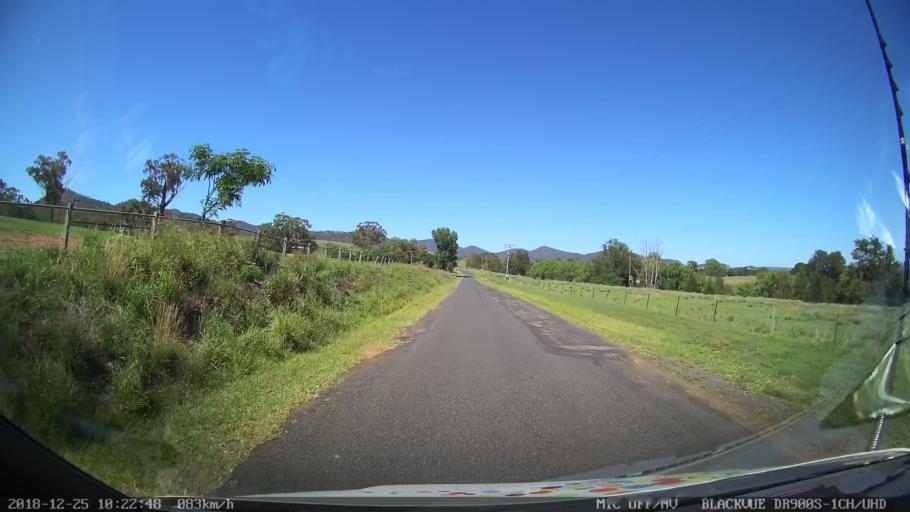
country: AU
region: New South Wales
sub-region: Muswellbrook
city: Denman
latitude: -32.3794
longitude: 150.5282
